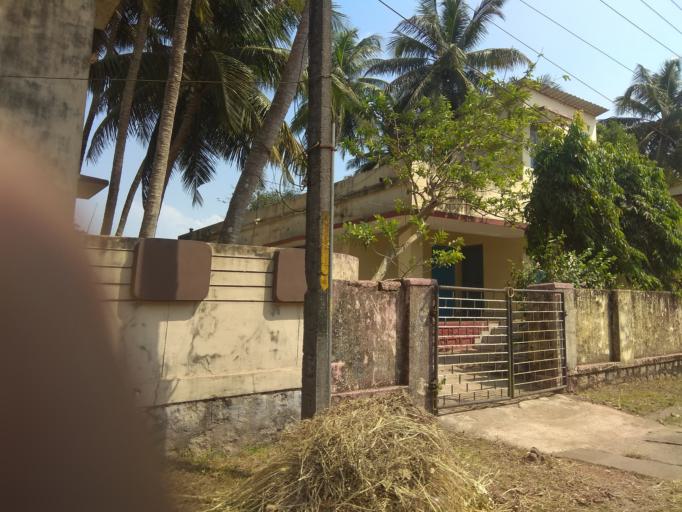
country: IN
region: Karnataka
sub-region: Dakshina Kannada
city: Mangalore
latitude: 12.9400
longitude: 74.8548
